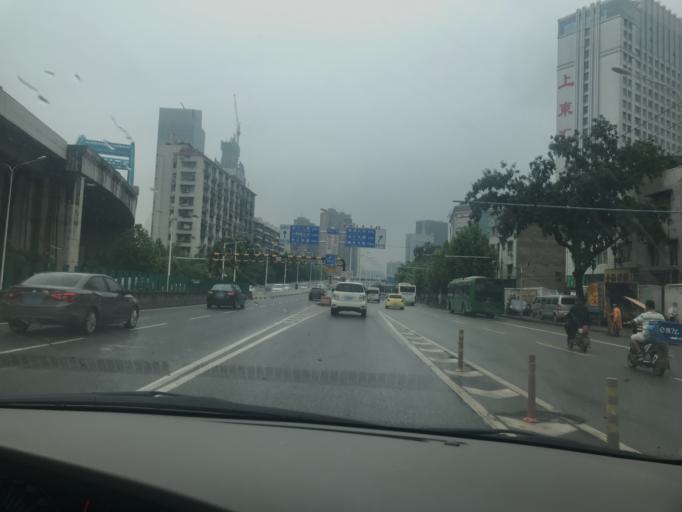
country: CN
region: Hubei
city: Jiang'an
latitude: 30.6187
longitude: 114.3071
